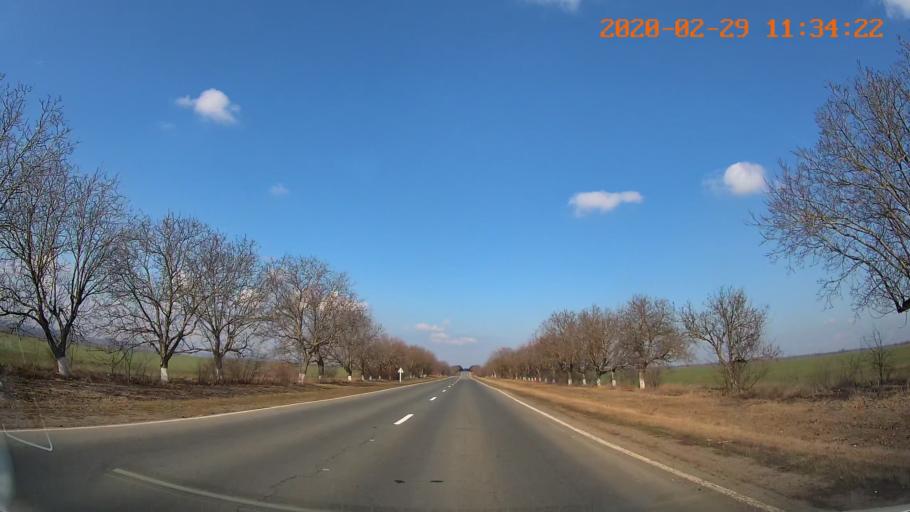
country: MD
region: Rezina
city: Saharna
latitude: 47.5648
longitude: 29.0745
